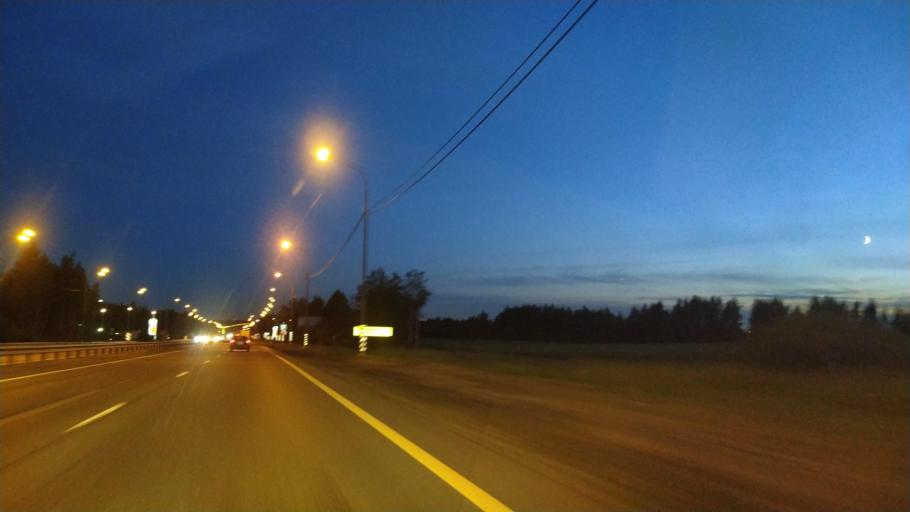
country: RU
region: Leningrad
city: Koltushi
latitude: 59.8944
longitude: 30.6600
